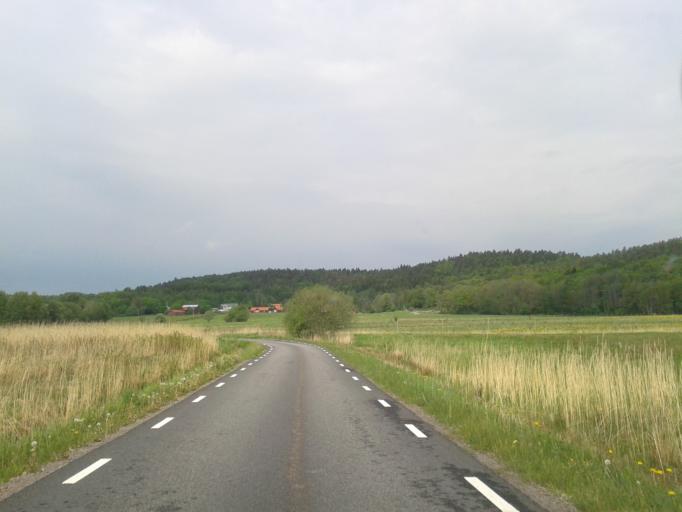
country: SE
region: Vaestra Goetaland
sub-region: Kungalvs Kommun
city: Diserod
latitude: 57.9271
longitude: 11.9694
